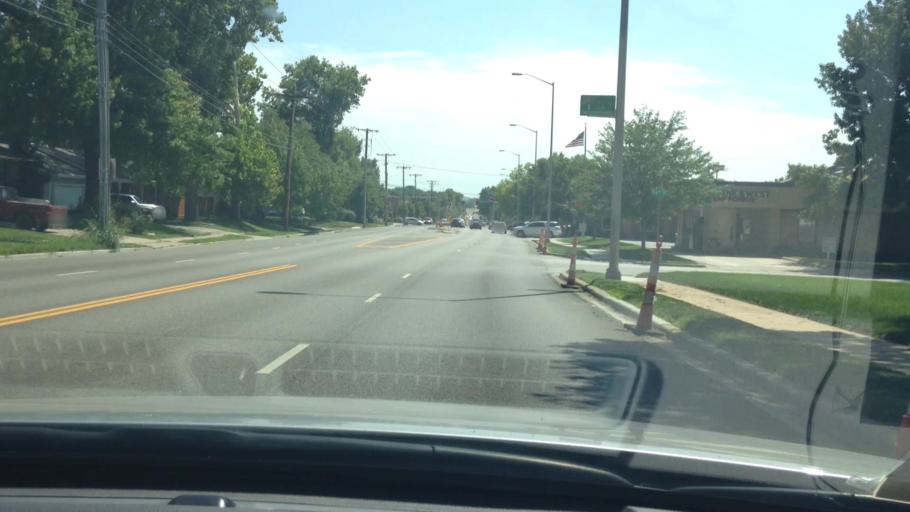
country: US
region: Kansas
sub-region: Johnson County
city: Overland Park
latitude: 38.9585
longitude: -94.6863
